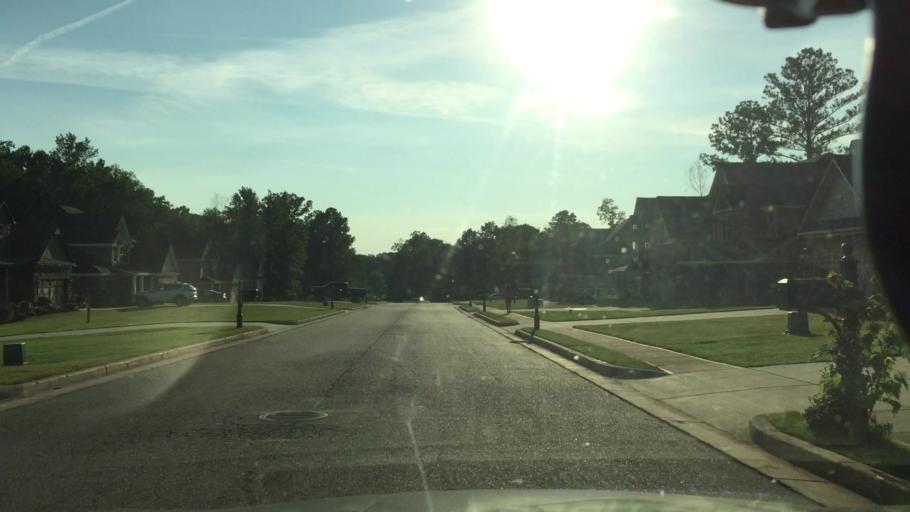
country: US
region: Alabama
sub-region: Lee County
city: Auburn
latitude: 32.5699
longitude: -85.4420
